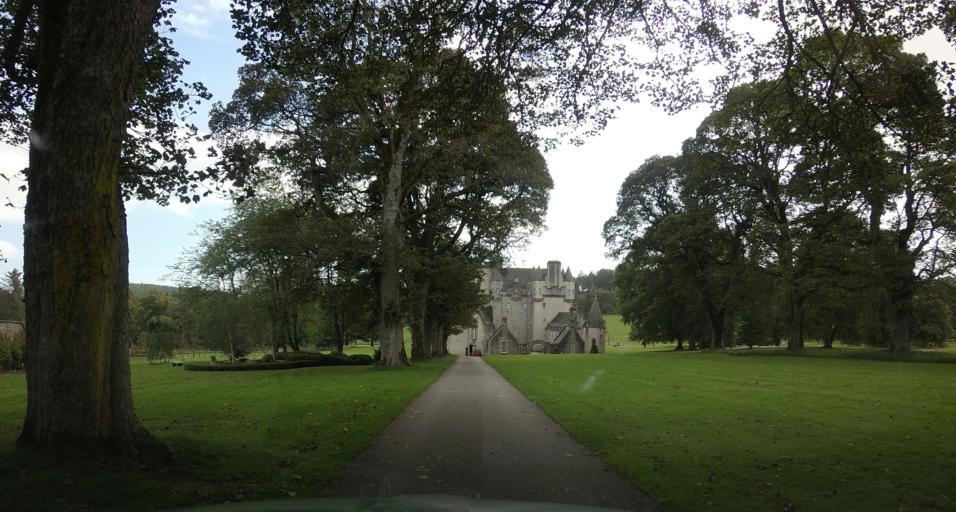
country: GB
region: Scotland
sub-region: Aberdeenshire
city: Kemnay
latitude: 57.2043
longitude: -2.4608
